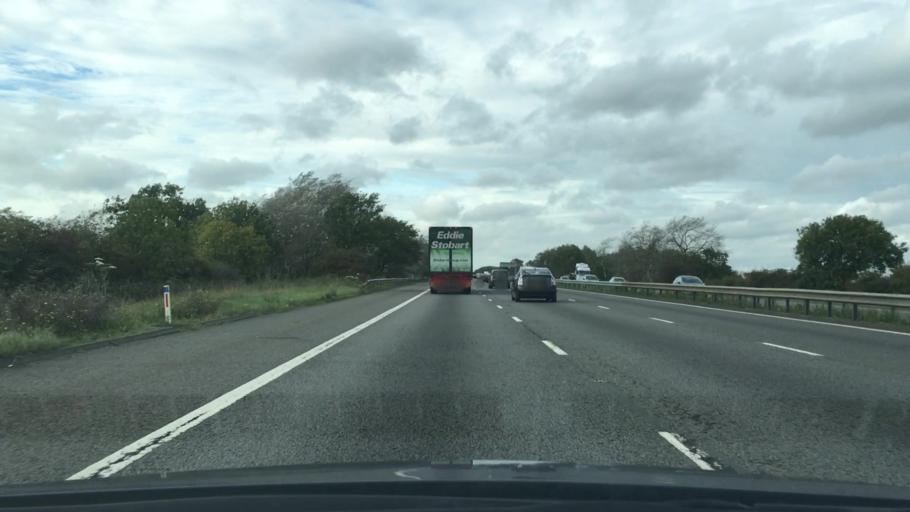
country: GB
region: England
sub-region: Milton Keynes
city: Hanslope
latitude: 52.1222
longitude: -0.8094
